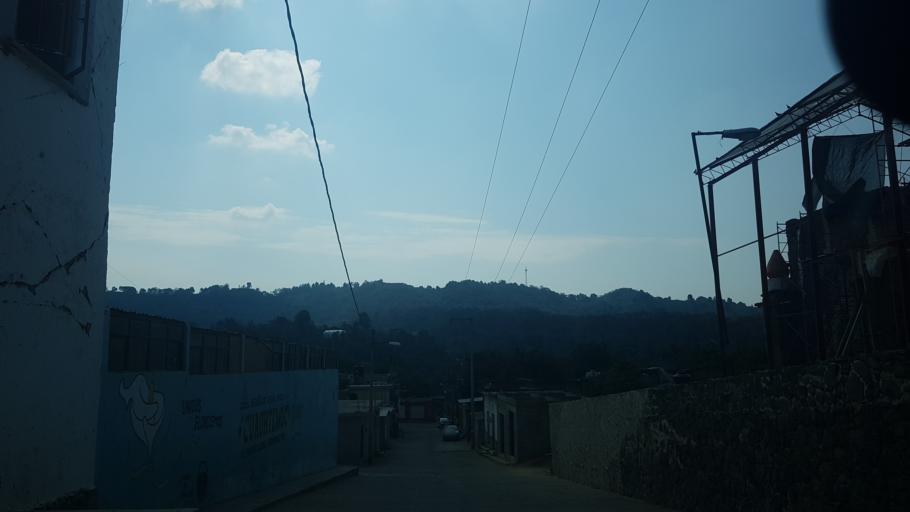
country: MX
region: Puebla
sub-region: Tochimilco
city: San Antonio Alpanocan
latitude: 18.8753
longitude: -98.7104
